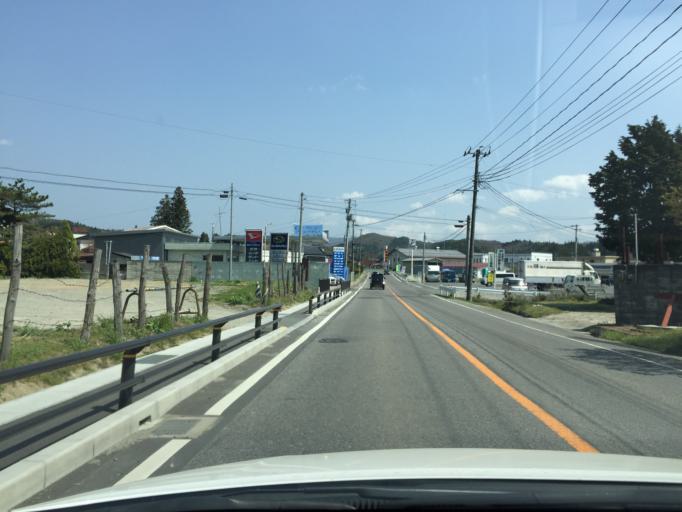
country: JP
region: Fukushima
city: Funehikimachi-funehiki
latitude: 37.4395
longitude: 140.6362
